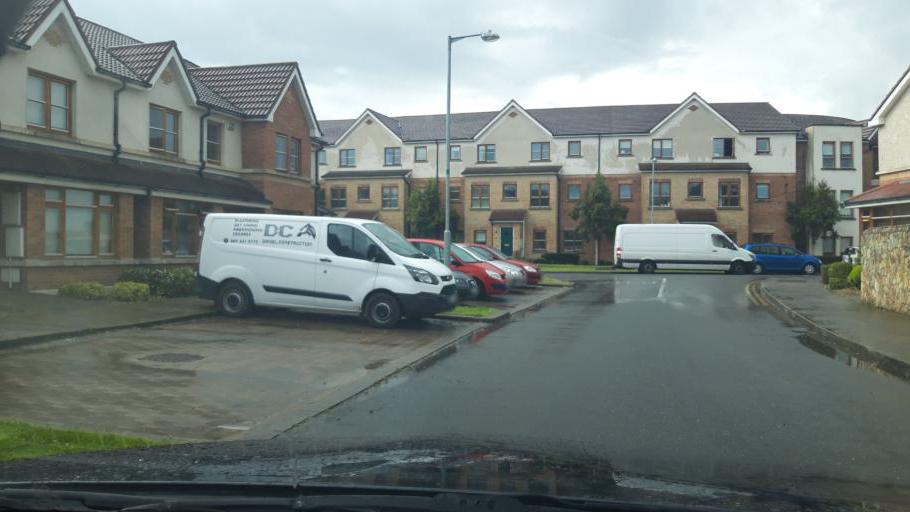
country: IE
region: Leinster
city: Hartstown
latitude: 53.4069
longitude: -6.4438
